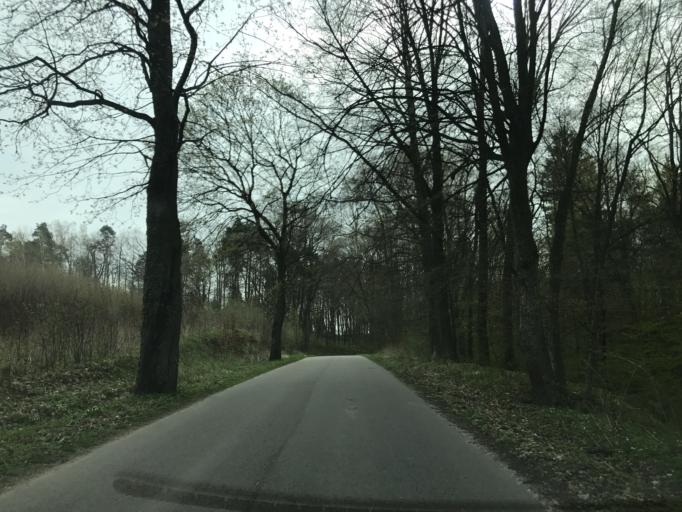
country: PL
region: Warmian-Masurian Voivodeship
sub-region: Powiat ostrodzki
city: Gierzwald
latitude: 53.6376
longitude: 20.0777
